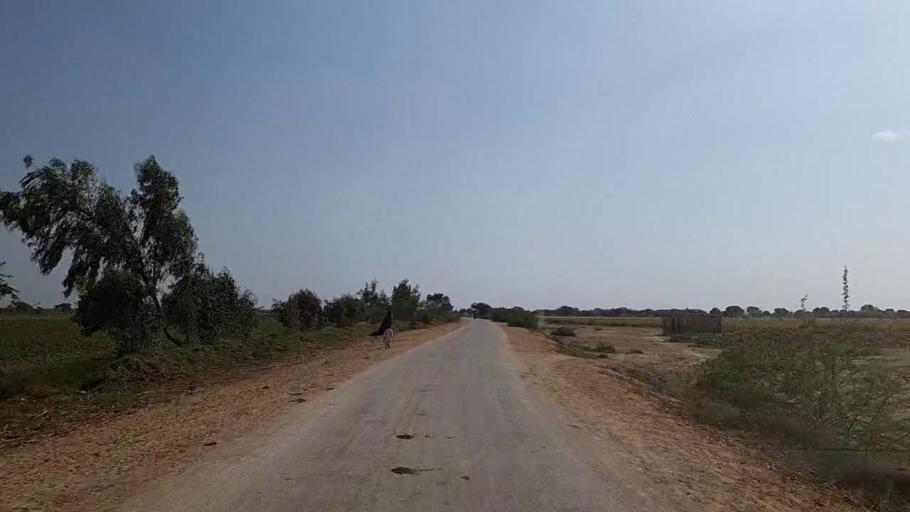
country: PK
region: Sindh
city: Daro Mehar
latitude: 24.7854
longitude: 68.1803
